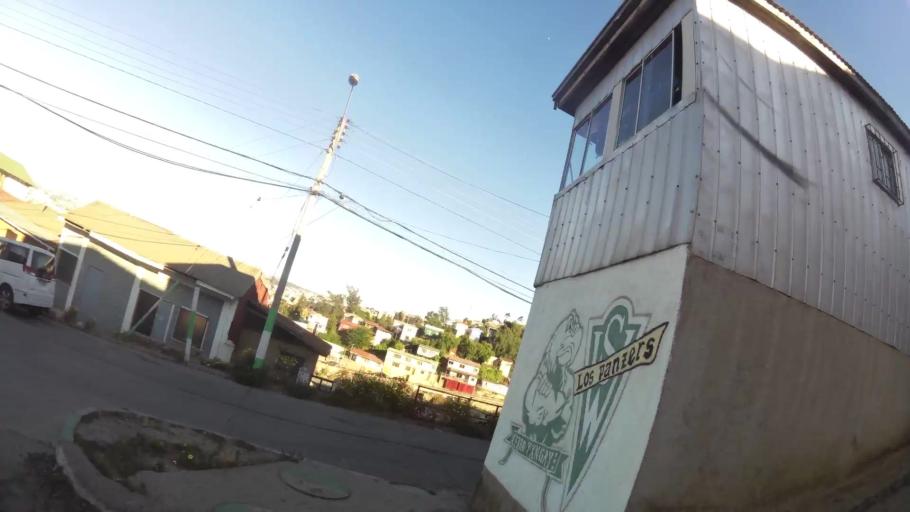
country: CL
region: Valparaiso
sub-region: Provincia de Valparaiso
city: Valparaiso
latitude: -33.0563
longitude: -71.6279
